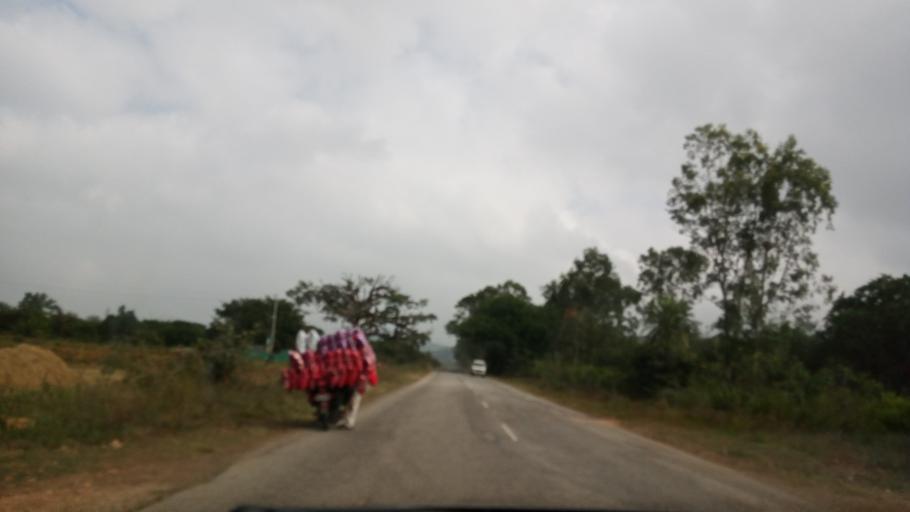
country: IN
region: Andhra Pradesh
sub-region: Chittoor
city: Madanapalle
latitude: 13.5002
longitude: 78.3288
